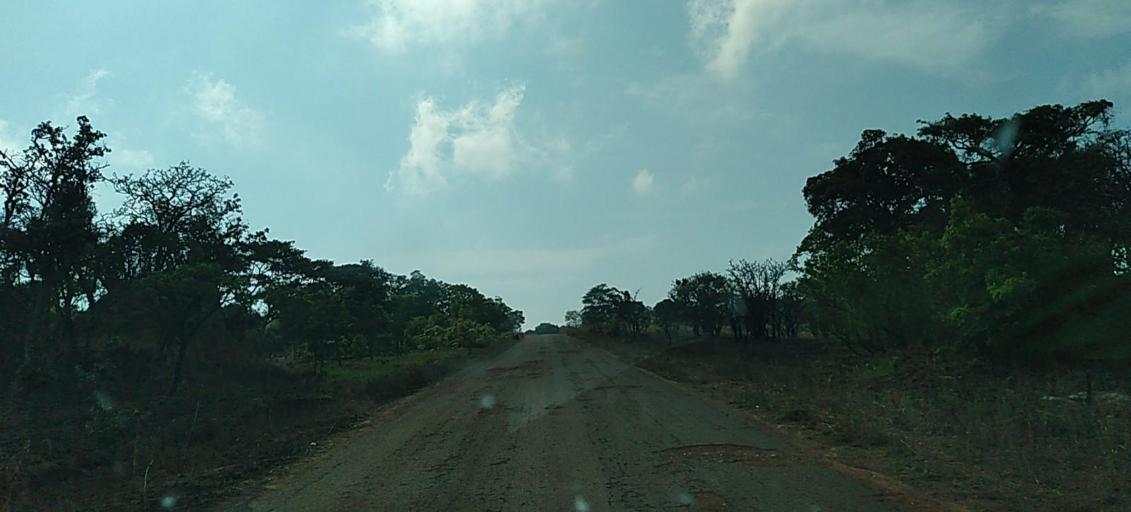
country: ZM
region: North-Western
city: Mwinilunga
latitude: -11.7706
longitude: 25.0096
